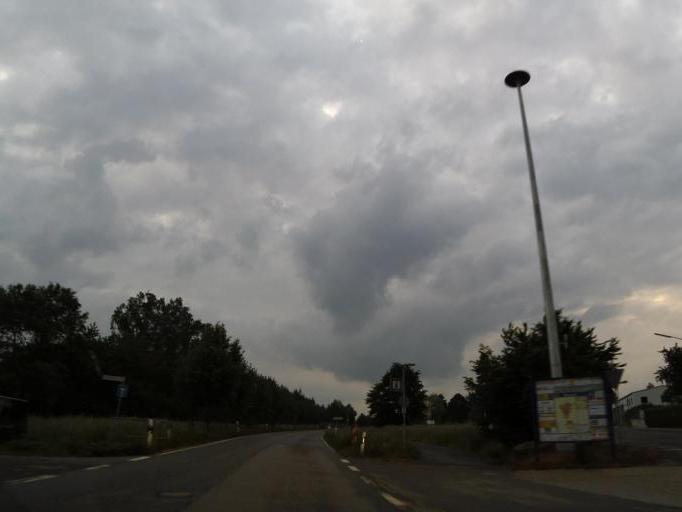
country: DE
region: Hesse
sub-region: Regierungsbezirk Darmstadt
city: Messel
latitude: 49.9227
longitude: 8.7440
